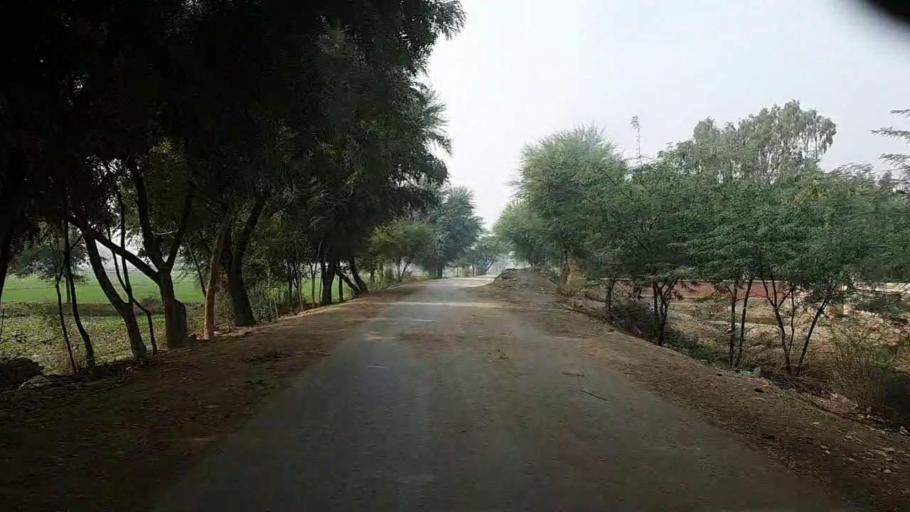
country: PK
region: Sindh
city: Kandiari
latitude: 26.9776
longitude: 68.5963
